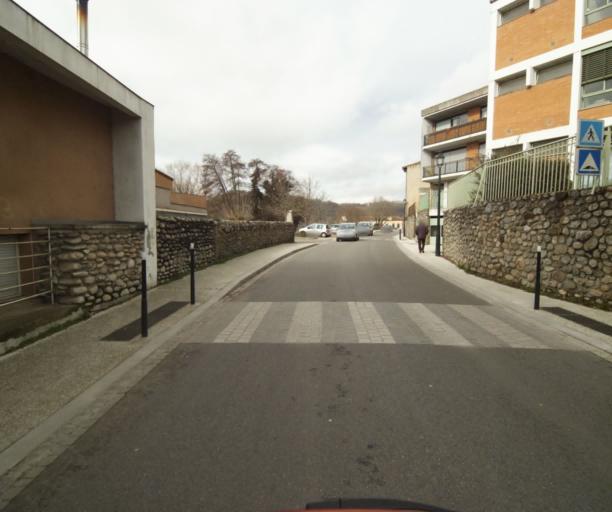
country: FR
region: Midi-Pyrenees
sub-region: Departement de l'Ariege
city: Pamiers
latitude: 43.1129
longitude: 1.6067
